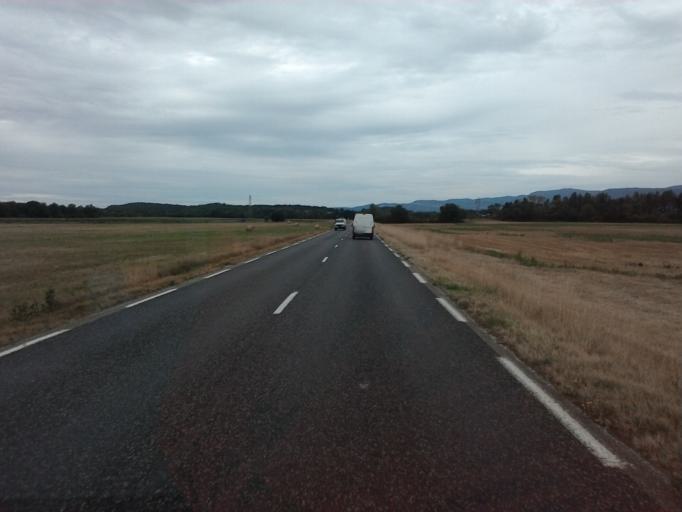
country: FR
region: Rhone-Alpes
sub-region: Departement de l'Isere
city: Bouvesse-Quirieu
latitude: 45.7451
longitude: 5.4045
